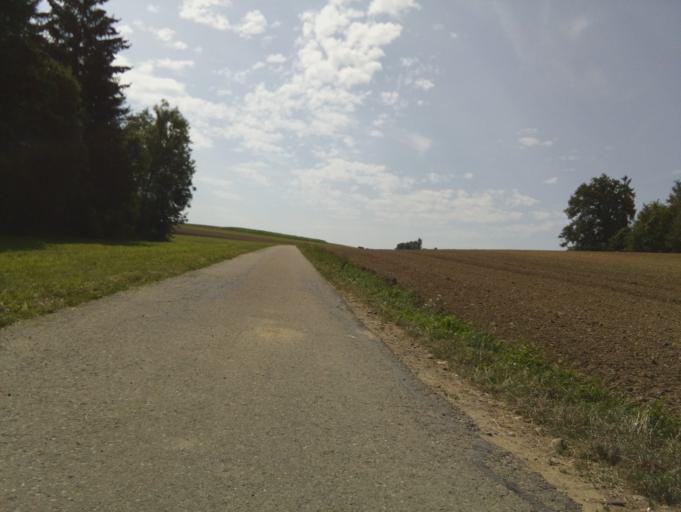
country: CH
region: Zurich
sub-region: Bezirk Andelfingen
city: Grossandelfingen
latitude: 47.5874
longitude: 8.6678
